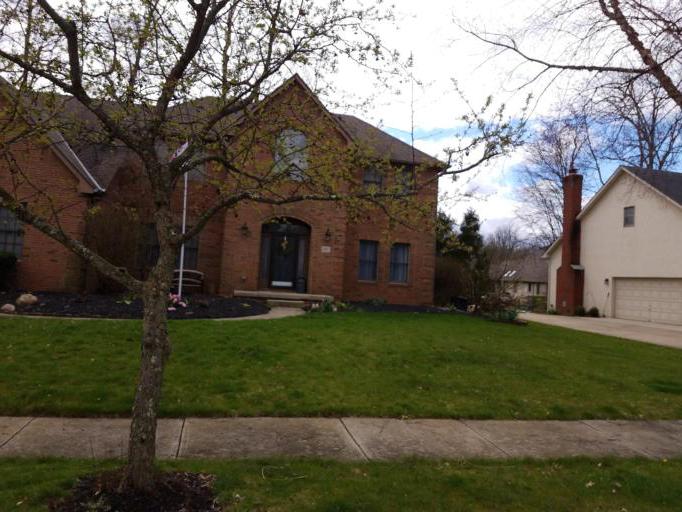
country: US
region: Ohio
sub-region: Franklin County
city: Westerville
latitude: 40.1397
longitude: -82.8932
